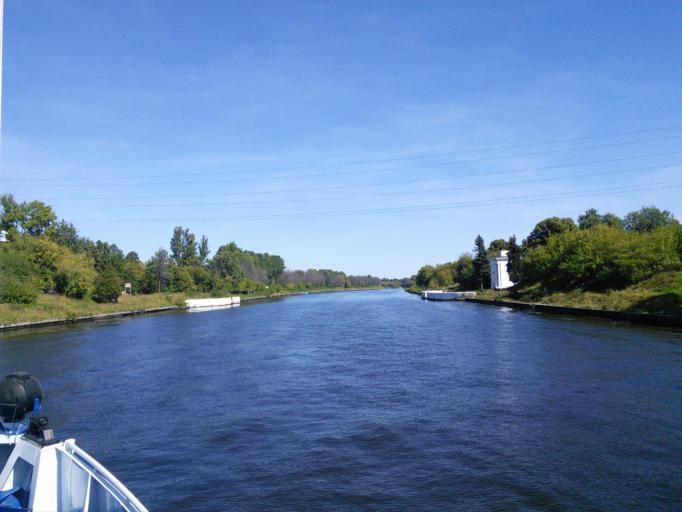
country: RU
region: Moskovskaya
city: Dolgoprudnyy
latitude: 55.9486
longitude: 37.4799
